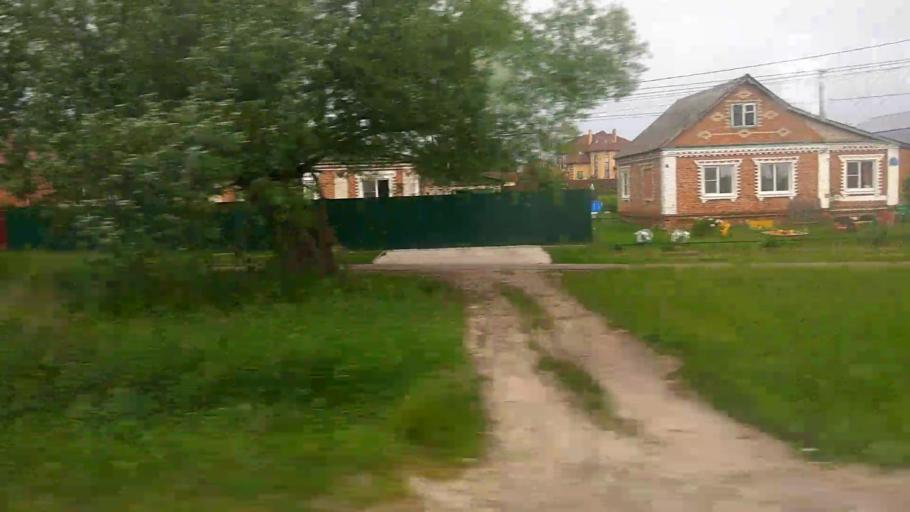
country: RU
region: Moskovskaya
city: Lukhovitsy
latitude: 54.9358
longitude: 39.0112
